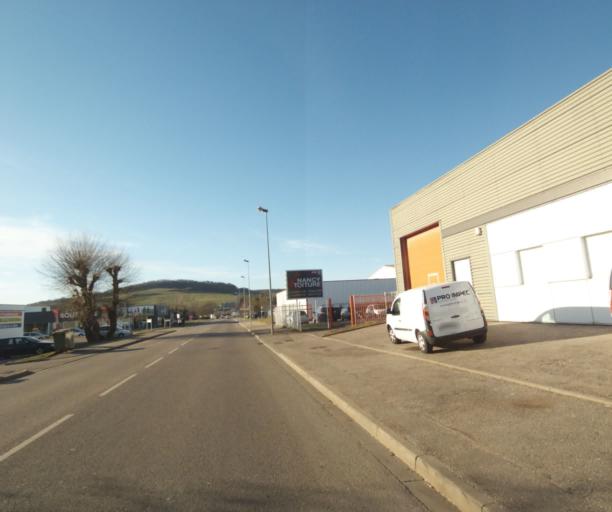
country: FR
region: Lorraine
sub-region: Departement de Meurthe-et-Moselle
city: Pulnoy
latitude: 48.7083
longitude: 6.2517
